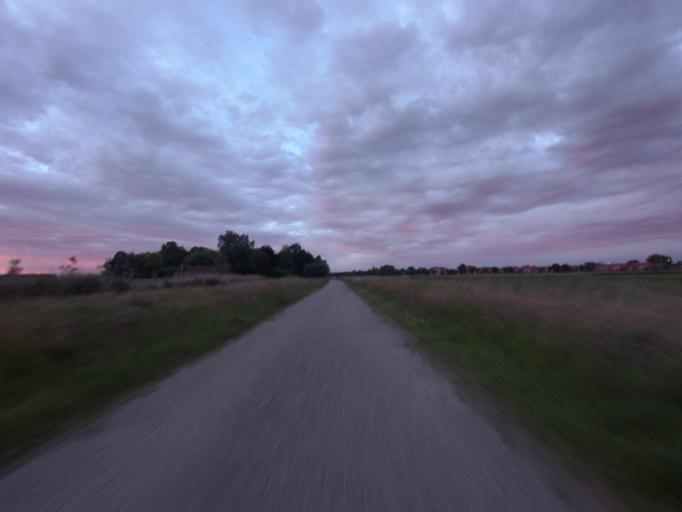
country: NL
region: North Holland
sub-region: Gemeente Ouder-Amstel
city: Ouderkerk aan de Amstel
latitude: 52.3023
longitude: 4.9082
